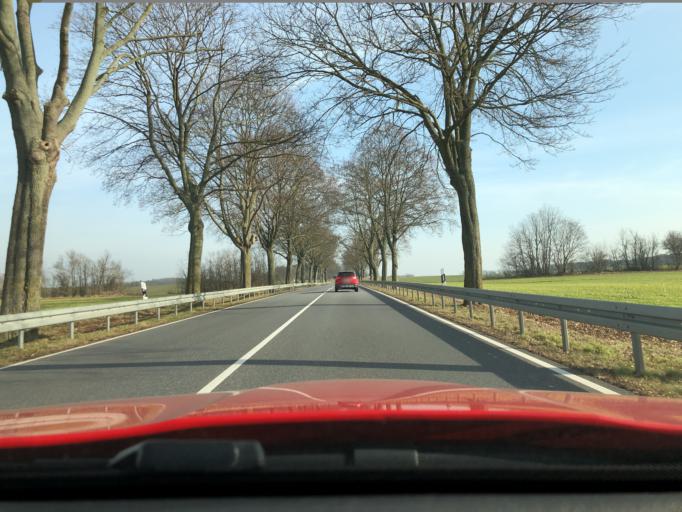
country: DE
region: Brandenburg
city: Muncheberg
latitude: 52.5048
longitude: 14.1893
